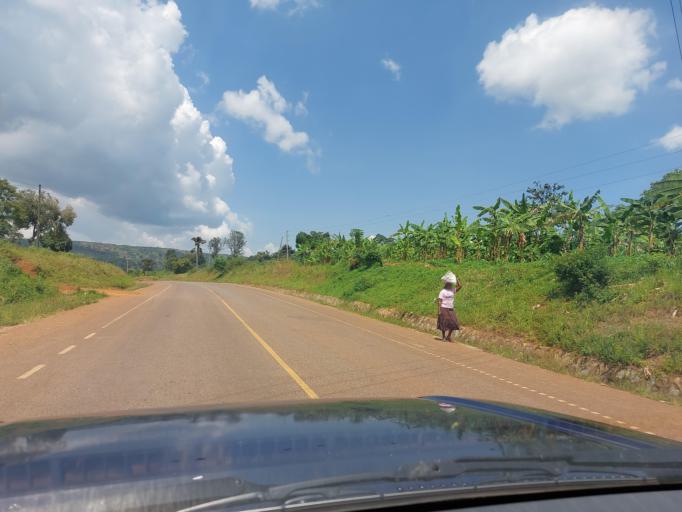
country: UG
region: Central Region
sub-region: Buikwe District
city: Buikwe
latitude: 0.3148
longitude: 33.1082
